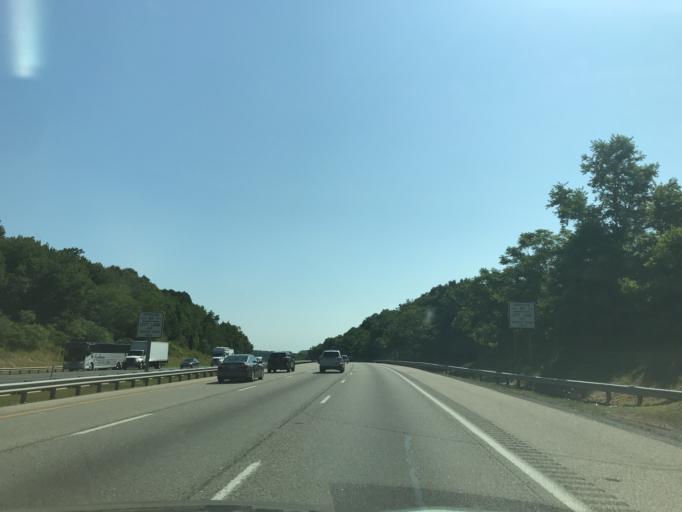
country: US
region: Maryland
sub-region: Cecil County
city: Perryville
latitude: 39.5991
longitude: -76.0481
